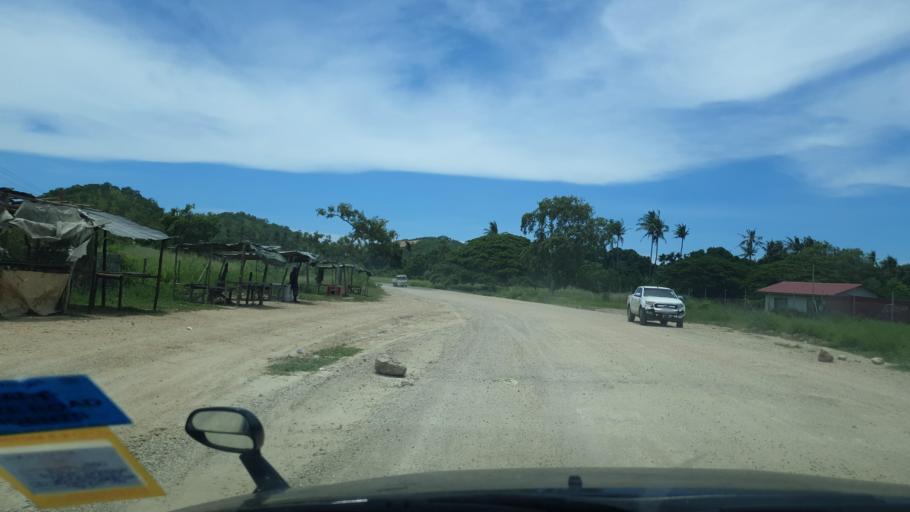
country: PG
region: National Capital
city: Port Moresby
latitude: -9.4243
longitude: 147.0745
